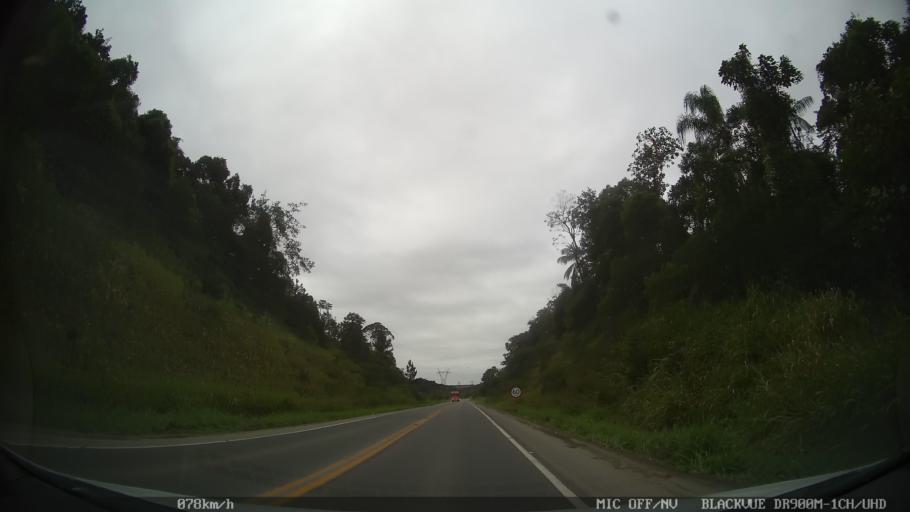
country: BR
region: Santa Catarina
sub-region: Joinville
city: Joinville
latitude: -26.2594
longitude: -48.9102
